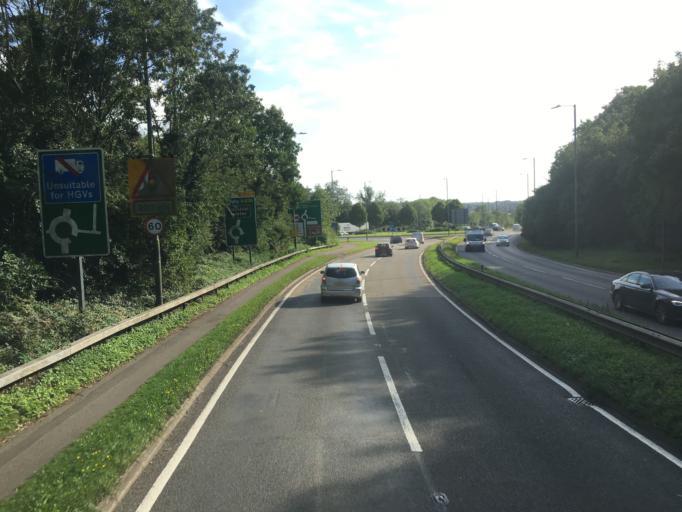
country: GB
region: England
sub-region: Warwickshire
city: Rugby
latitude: 52.3962
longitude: -1.2482
